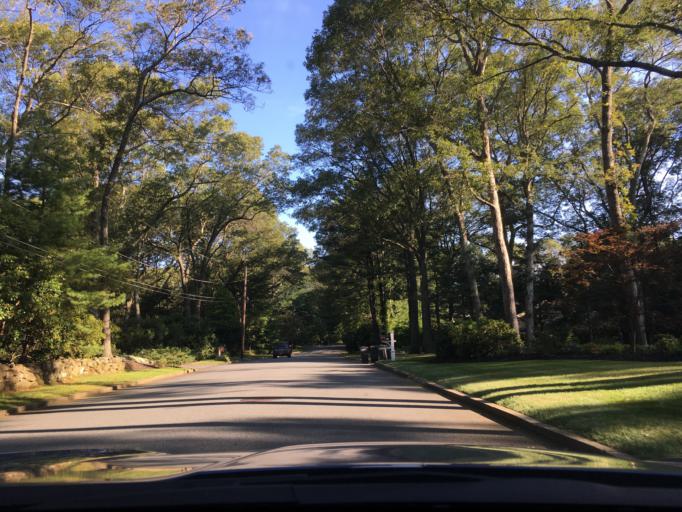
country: US
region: Rhode Island
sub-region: Kent County
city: East Greenwich
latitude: 41.6436
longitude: -71.4848
